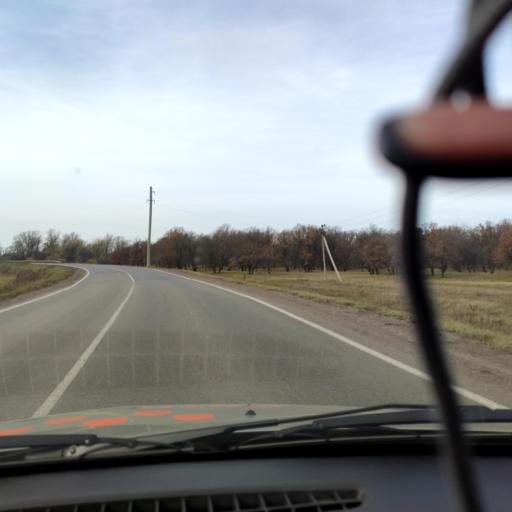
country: RU
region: Bashkortostan
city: Kabakovo
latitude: 54.5666
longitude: 55.9881
